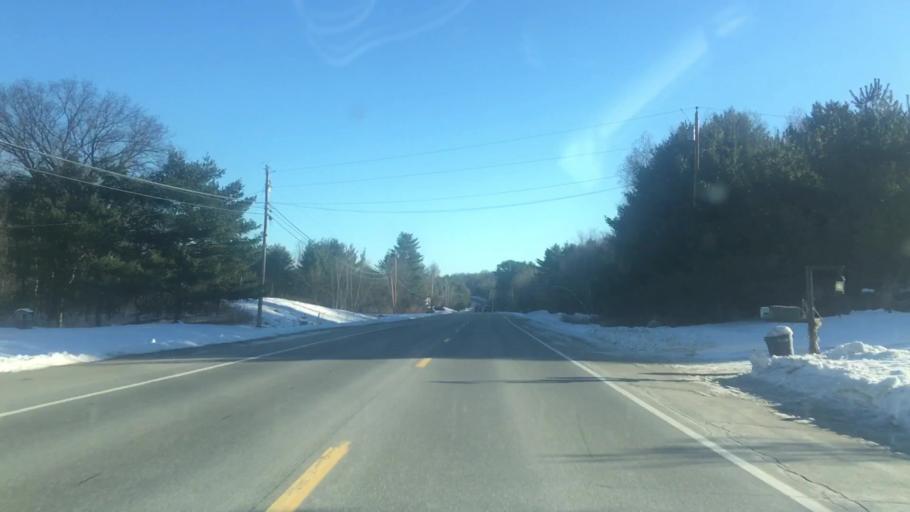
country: US
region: Maine
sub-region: Somerset County
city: Norridgewock
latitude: 44.6787
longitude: -69.7232
